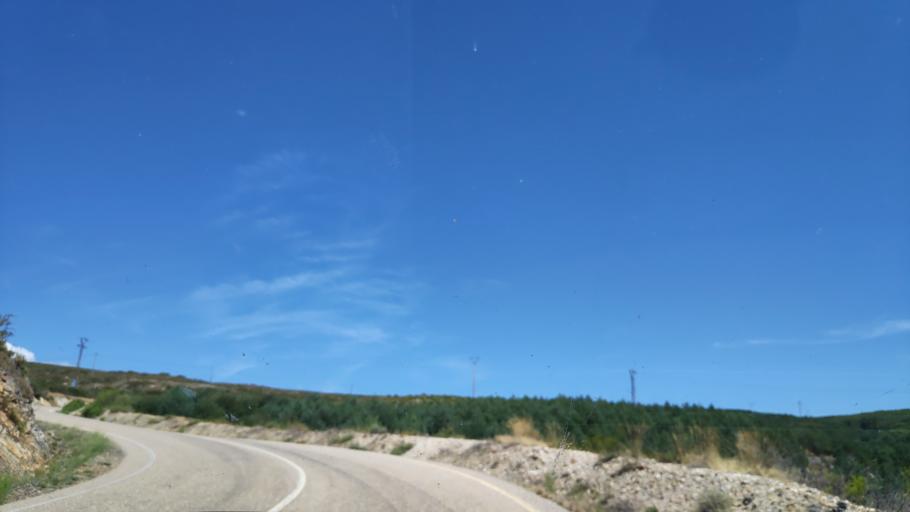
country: ES
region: Castille and Leon
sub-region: Provincia de Zamora
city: Requejo
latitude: 42.0054
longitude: -6.6954
